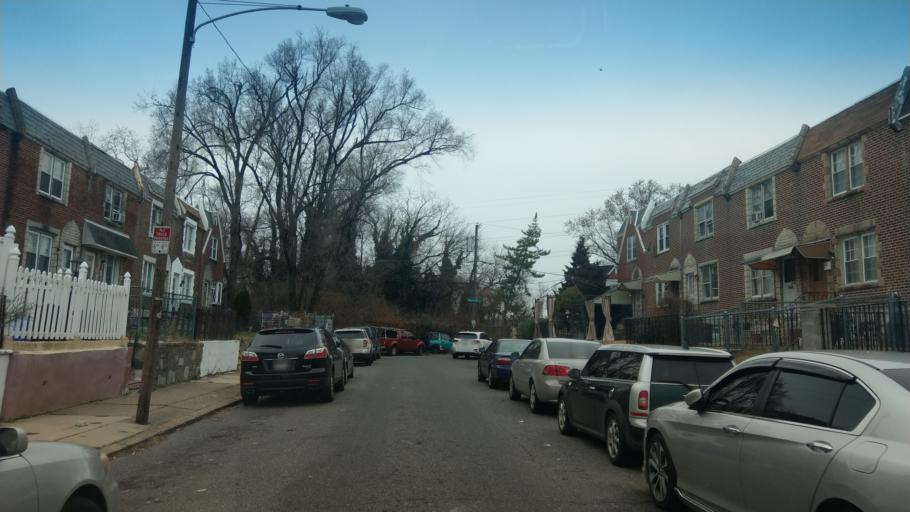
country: US
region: Pennsylvania
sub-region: Montgomery County
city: Rockledge
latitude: 40.0174
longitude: -75.1128
